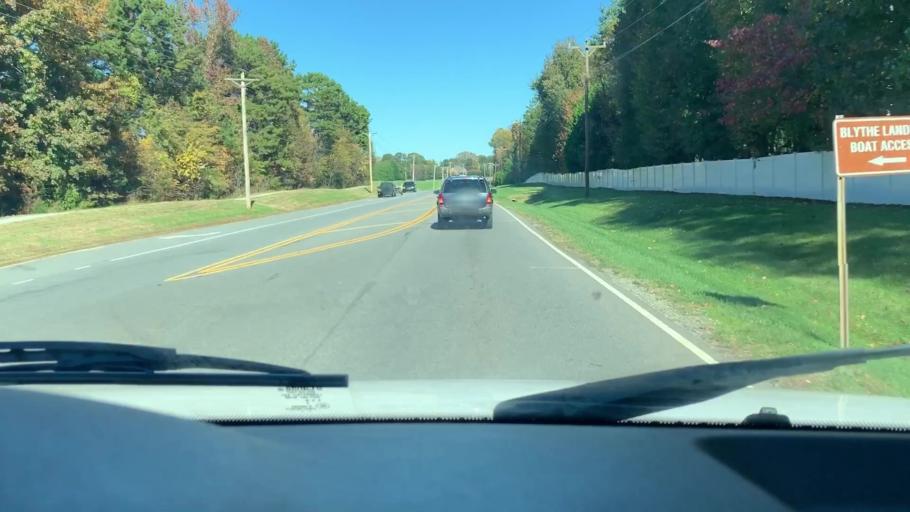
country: US
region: North Carolina
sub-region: Mecklenburg County
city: Huntersville
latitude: 35.4358
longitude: -80.9041
